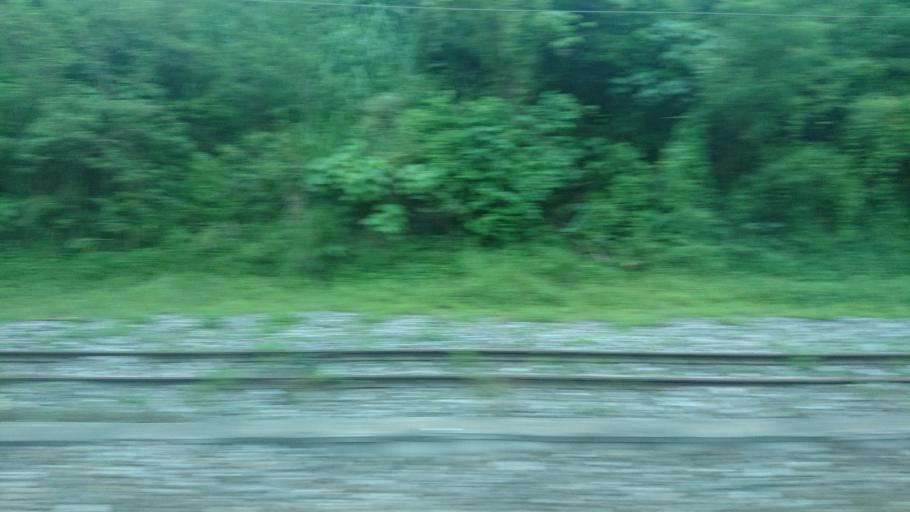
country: TW
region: Taiwan
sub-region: Hualien
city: Hualian
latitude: 24.1242
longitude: 121.6386
